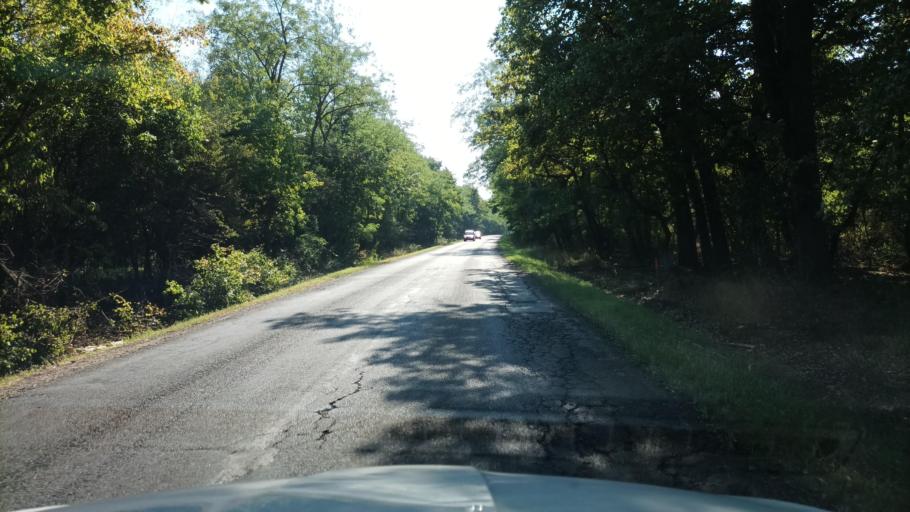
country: HU
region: Pest
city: Isaszeg
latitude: 47.5722
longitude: 19.4382
